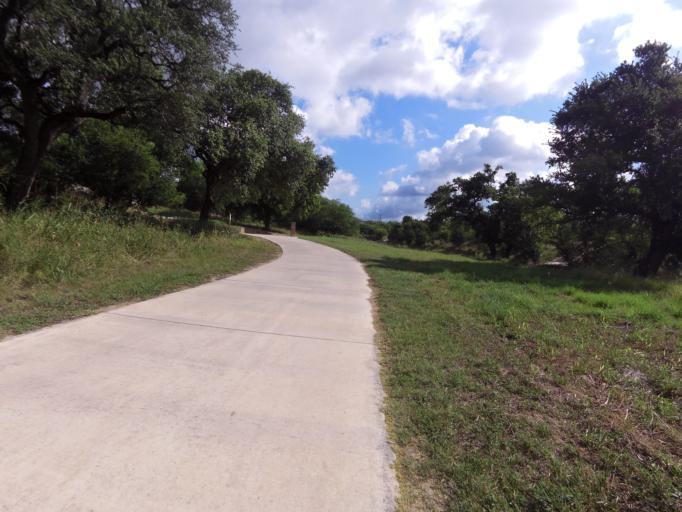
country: US
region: Texas
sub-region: Bexar County
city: Shavano Park
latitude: 29.5763
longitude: -98.6075
